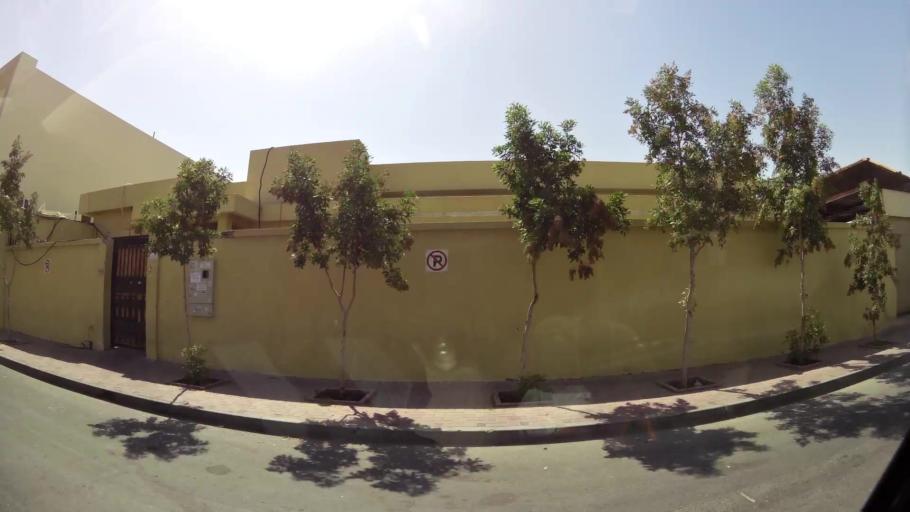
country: AE
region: Ash Shariqah
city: Sharjah
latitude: 25.2339
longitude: 55.2712
